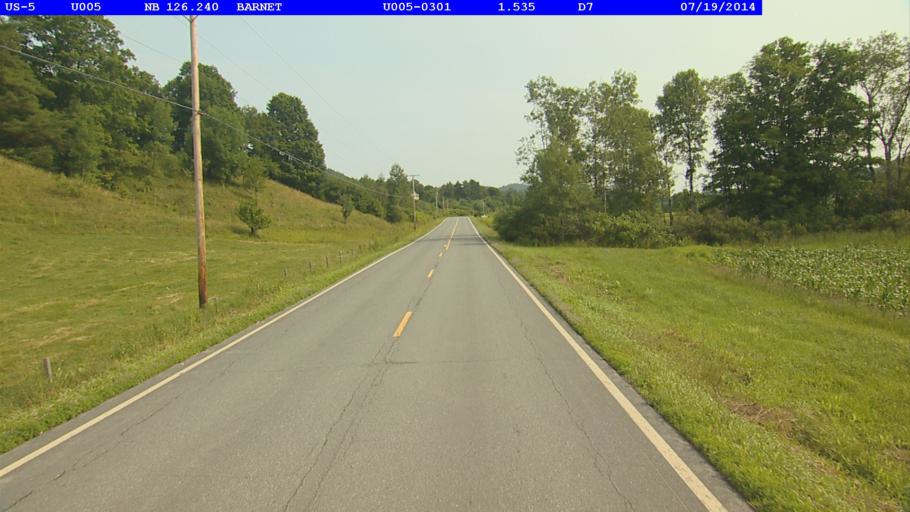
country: US
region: New Hampshire
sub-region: Grafton County
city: Woodsville
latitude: 44.2769
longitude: -72.0677
